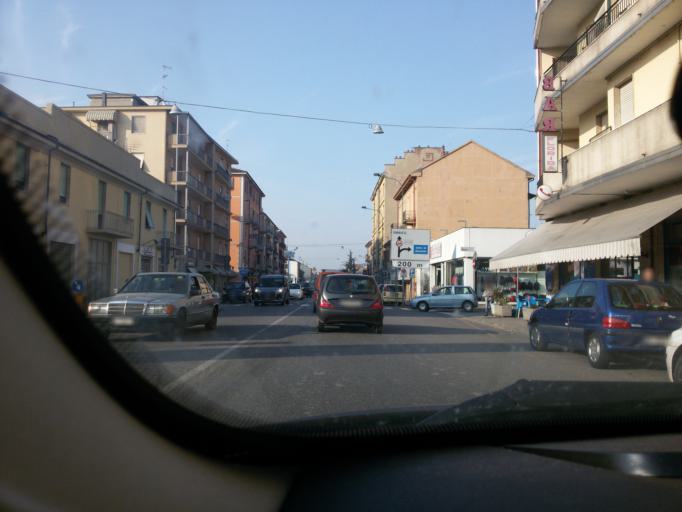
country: IT
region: Piedmont
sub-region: Provincia di Alessandria
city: Casale Monferrato
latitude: 45.1224
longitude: 8.4511
